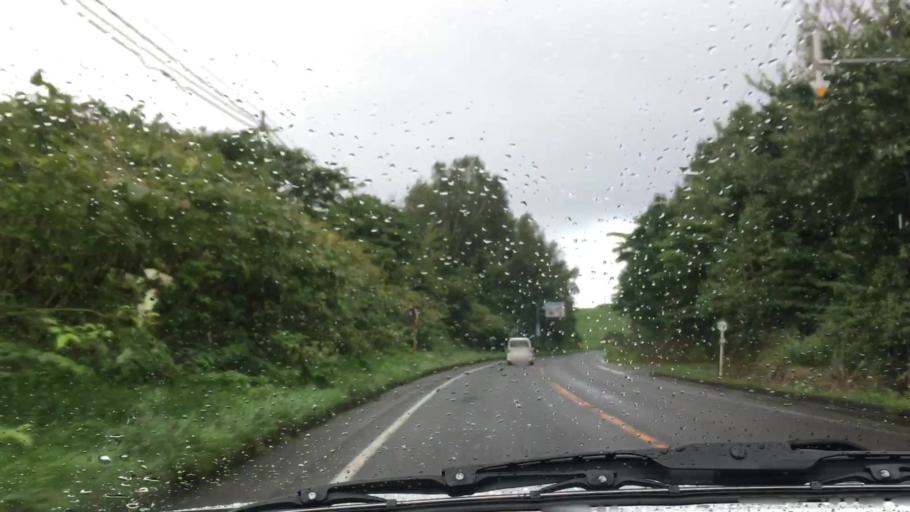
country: JP
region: Hokkaido
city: Niseko Town
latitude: 42.5969
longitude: 140.7219
